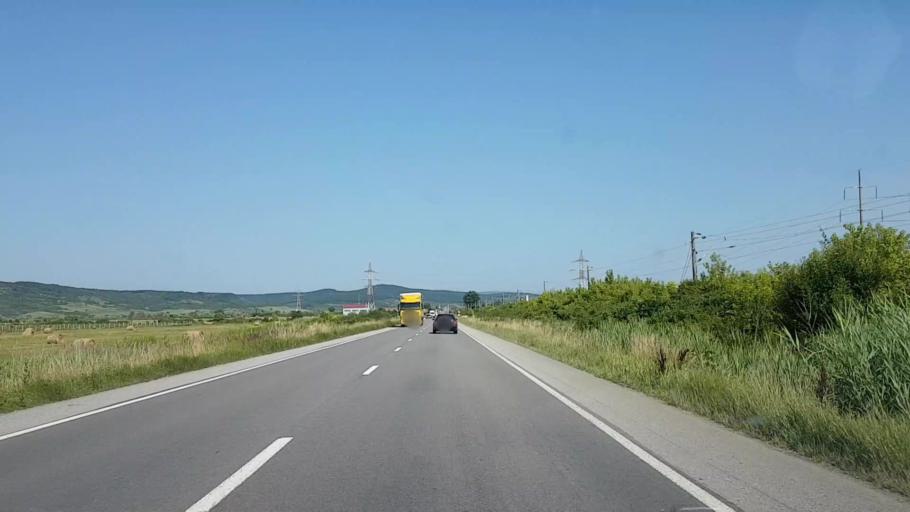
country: RO
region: Bistrita-Nasaud
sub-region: Comuna Sintereag
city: Cociu
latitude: 47.1819
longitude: 24.2489
